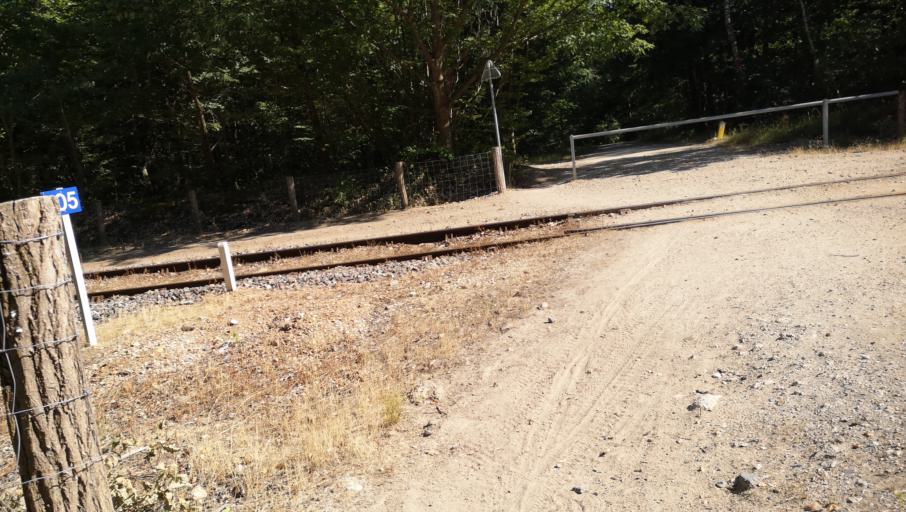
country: FR
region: Centre
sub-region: Departement du Loiret
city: Marigny-les-Usages
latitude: 47.9443
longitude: 1.9940
